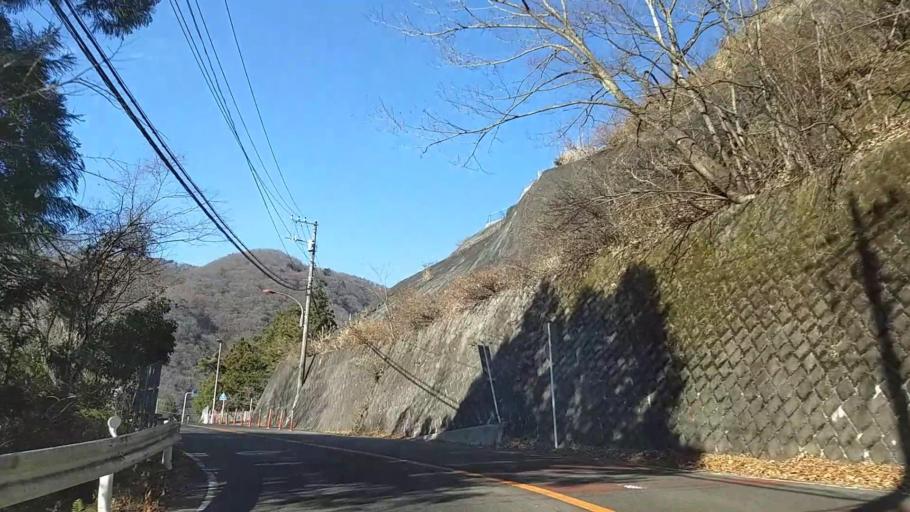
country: JP
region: Yamanashi
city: Uenohara
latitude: 35.5418
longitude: 139.1239
